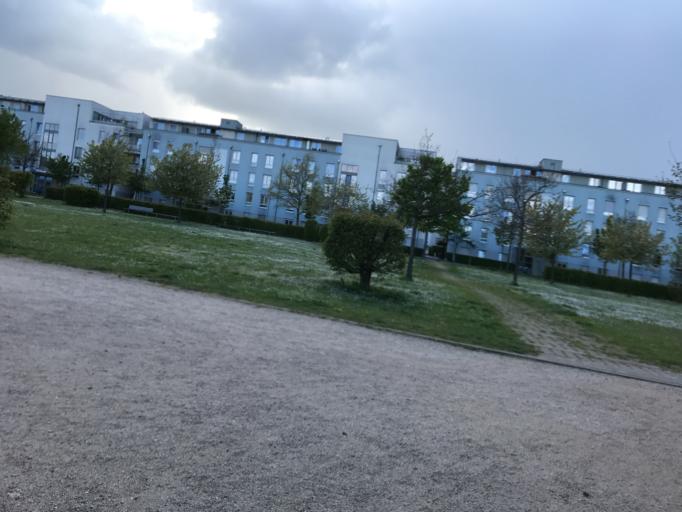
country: DE
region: Rheinland-Pfalz
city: Budenheim
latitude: 50.0089
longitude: 8.2196
